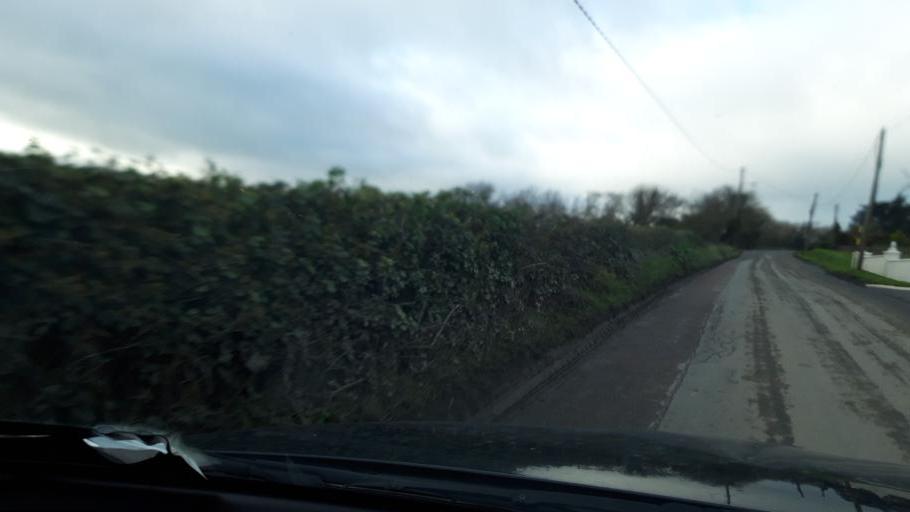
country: IE
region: Leinster
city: An Ros
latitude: 53.5500
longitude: -6.1198
